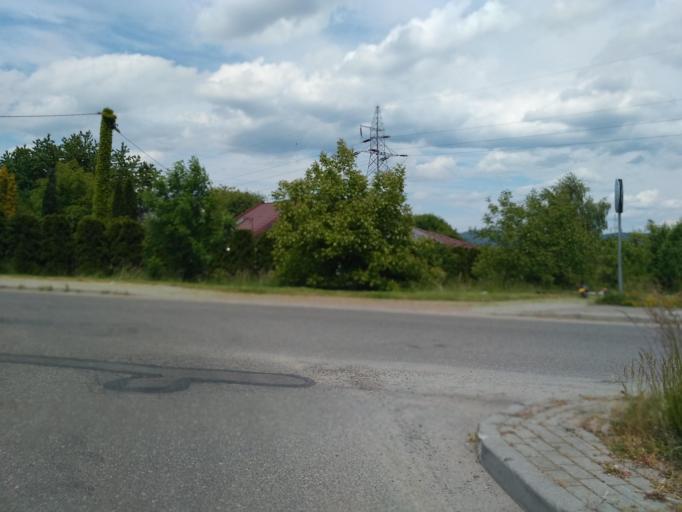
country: PL
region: Subcarpathian Voivodeship
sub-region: Powiat krosnienski
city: Odrzykon
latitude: 49.7099
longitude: 21.7301
